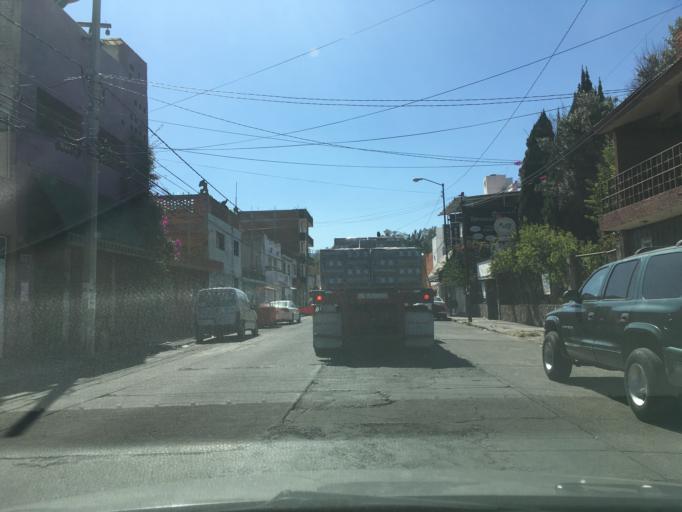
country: MX
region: Michoacan
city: Morelia
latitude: 19.6920
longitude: -101.1879
